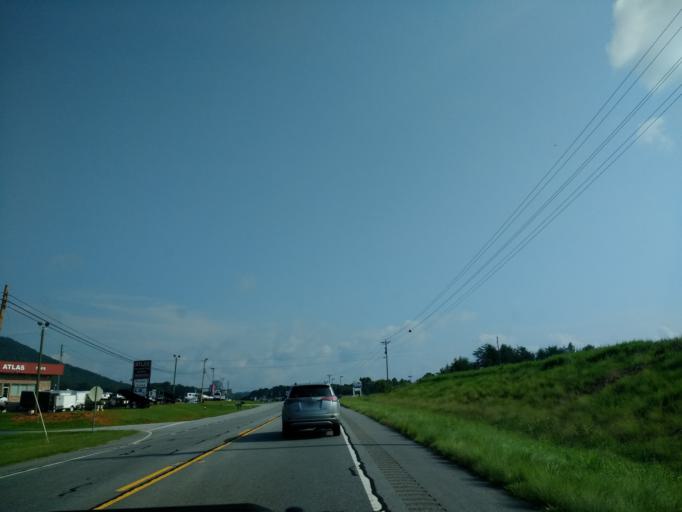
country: US
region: Georgia
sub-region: White County
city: Cleveland
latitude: 34.5538
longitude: -83.7610
